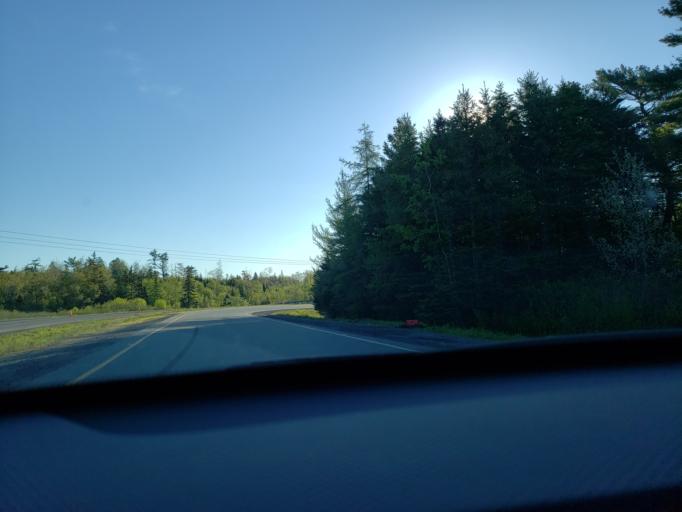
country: CA
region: Nova Scotia
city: Cole Harbour
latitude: 44.7139
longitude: -63.3947
